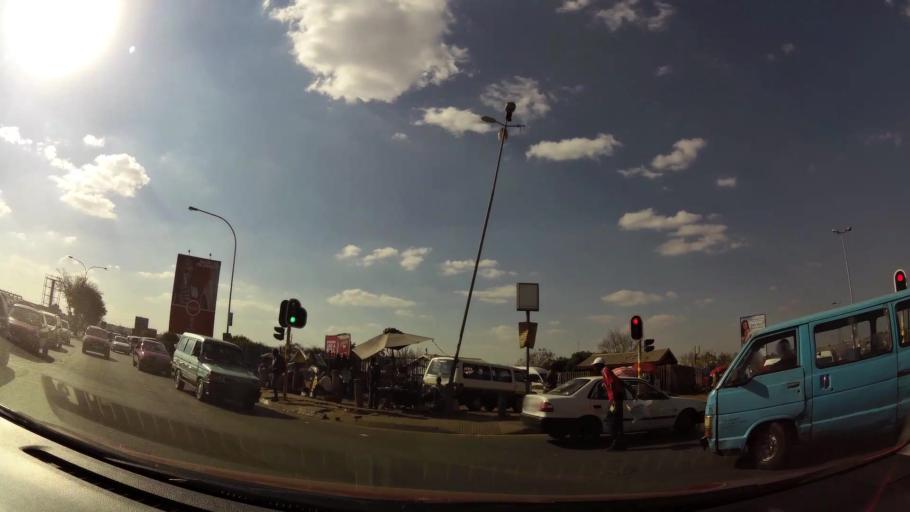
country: ZA
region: Gauteng
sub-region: City of Johannesburg Metropolitan Municipality
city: Roodepoort
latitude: -26.2146
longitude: 27.8709
